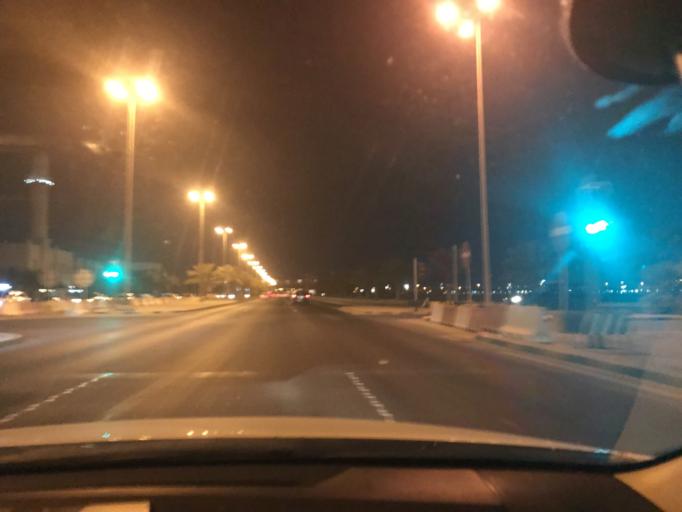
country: BH
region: Muharraq
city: Al Muharraq
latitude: 26.2618
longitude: 50.6347
